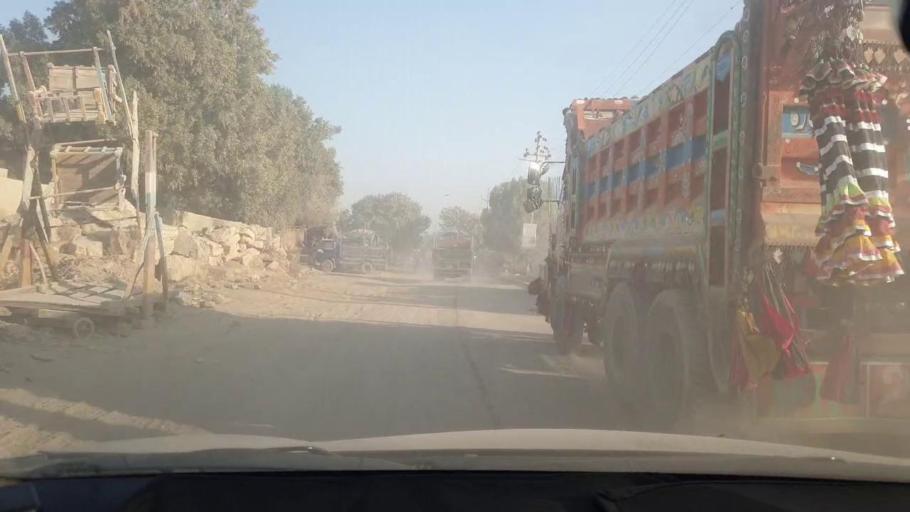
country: PK
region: Sindh
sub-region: Karachi District
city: Karachi
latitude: 24.9737
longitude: 67.0399
